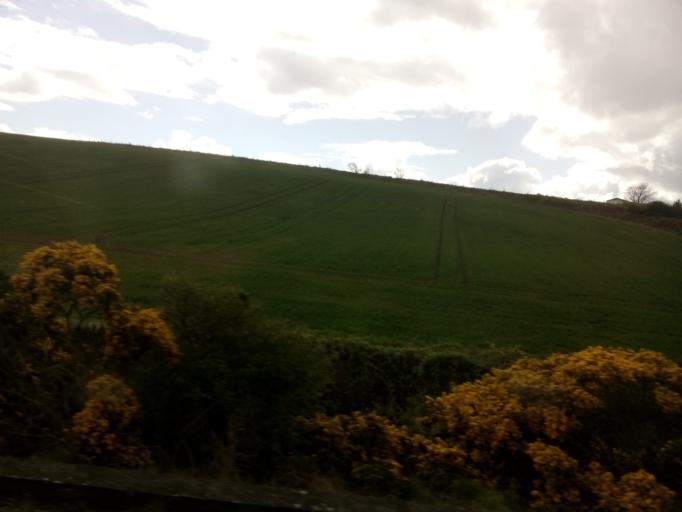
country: GB
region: England
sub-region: Northumberland
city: Berwick-Upon-Tweed
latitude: 55.7524
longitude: -1.9878
